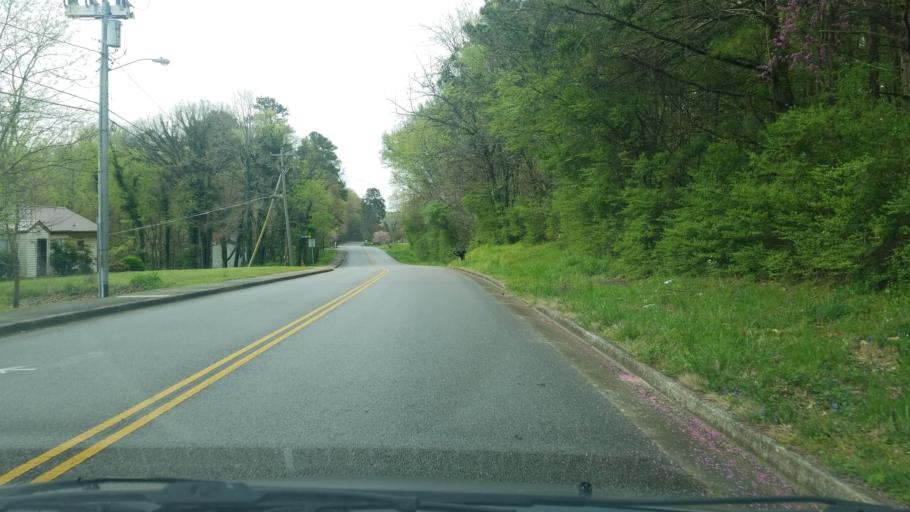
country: US
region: Tennessee
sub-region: Hamilton County
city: Collegedale
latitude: 35.0381
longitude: -85.0569
